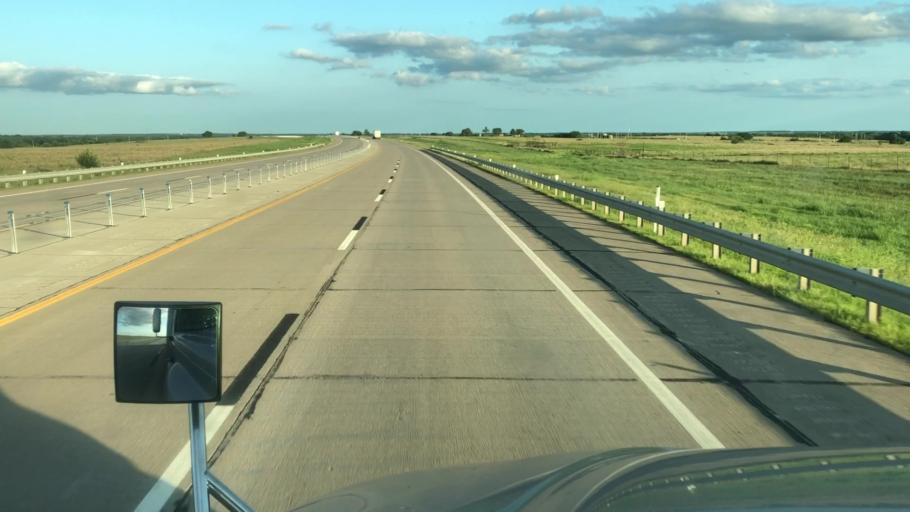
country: US
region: Oklahoma
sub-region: Pawnee County
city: Pawnee
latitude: 36.3421
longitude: -97.0247
